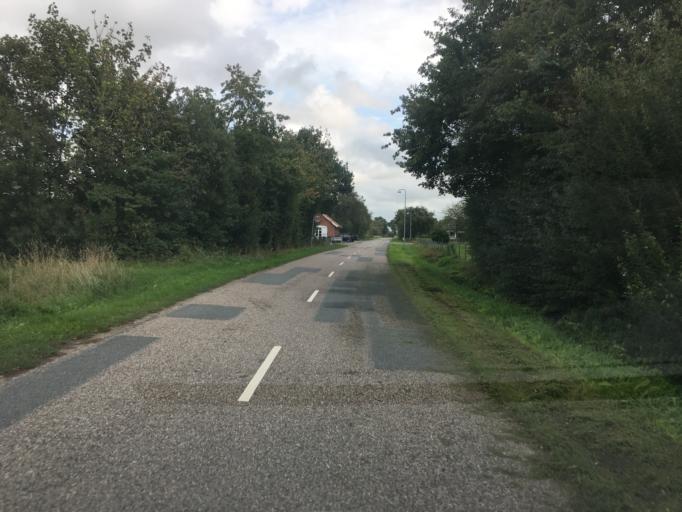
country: DE
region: Schleswig-Holstein
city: Aventoft
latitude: 54.9587
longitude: 8.8128
